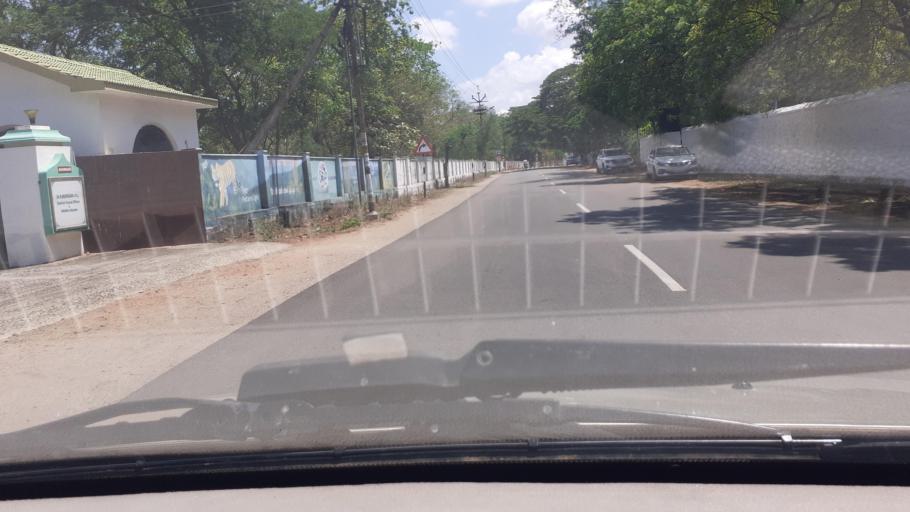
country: IN
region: Tamil Nadu
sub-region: Tirunelveli Kattabo
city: Tirunelveli
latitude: 8.7183
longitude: 77.7458
